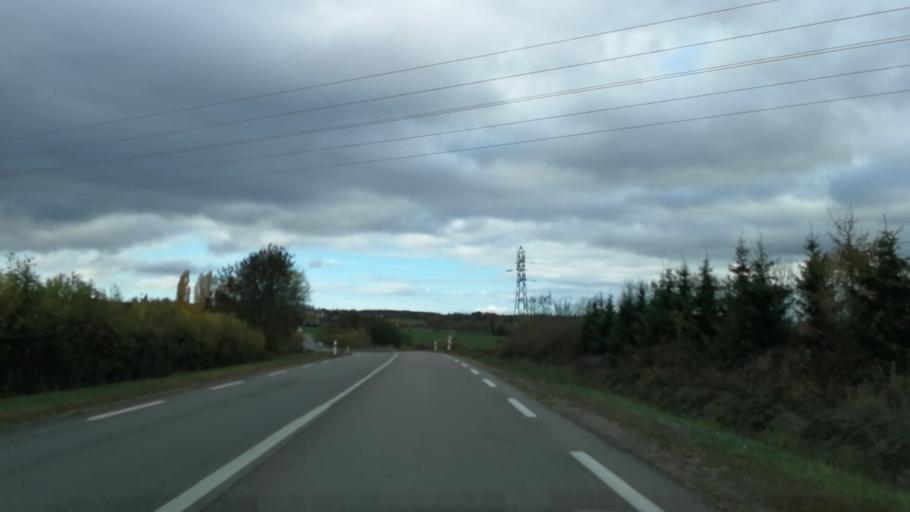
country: FR
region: Bourgogne
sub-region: Departement de la Cote-d'Or
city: Saulieu
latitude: 47.2686
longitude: 4.2561
